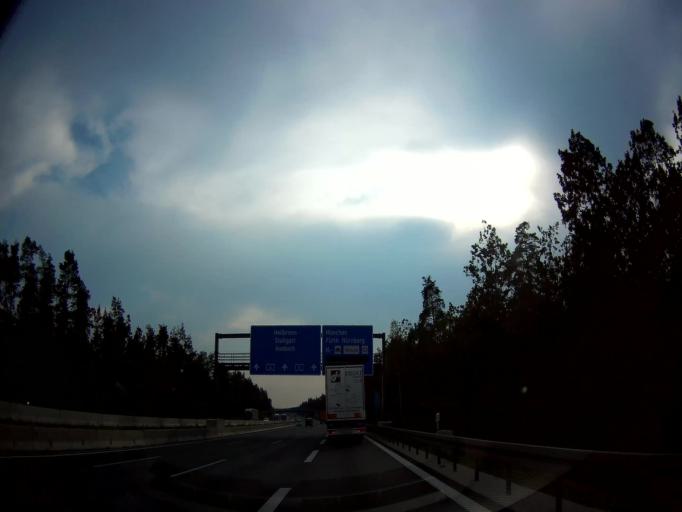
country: DE
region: Bavaria
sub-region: Regierungsbezirk Mittelfranken
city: Wendelstein
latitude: 49.3895
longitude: 11.1565
